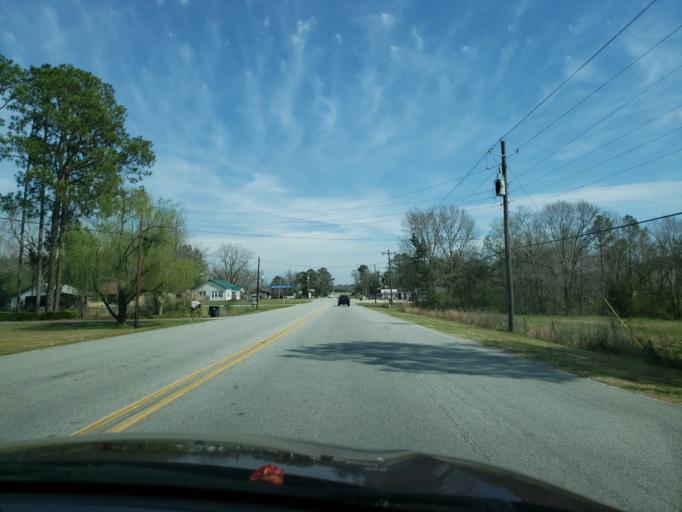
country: US
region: Alabama
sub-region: Elmore County
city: Tallassee
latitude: 32.5515
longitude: -85.8434
